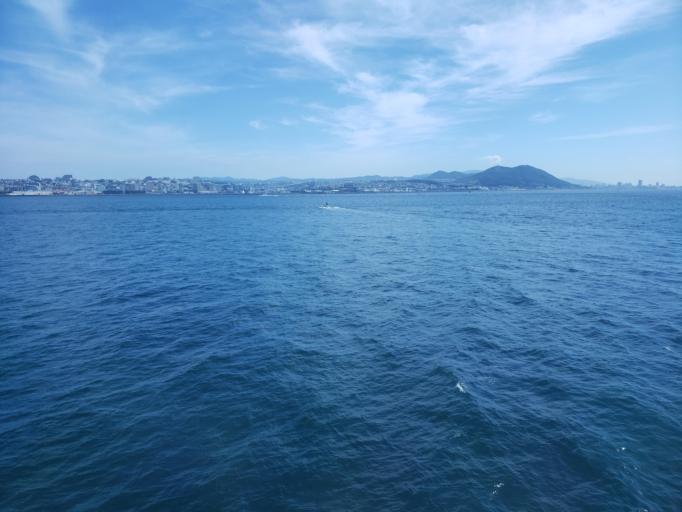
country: JP
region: Hyogo
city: Akashi
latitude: 34.6059
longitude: 135.0474
